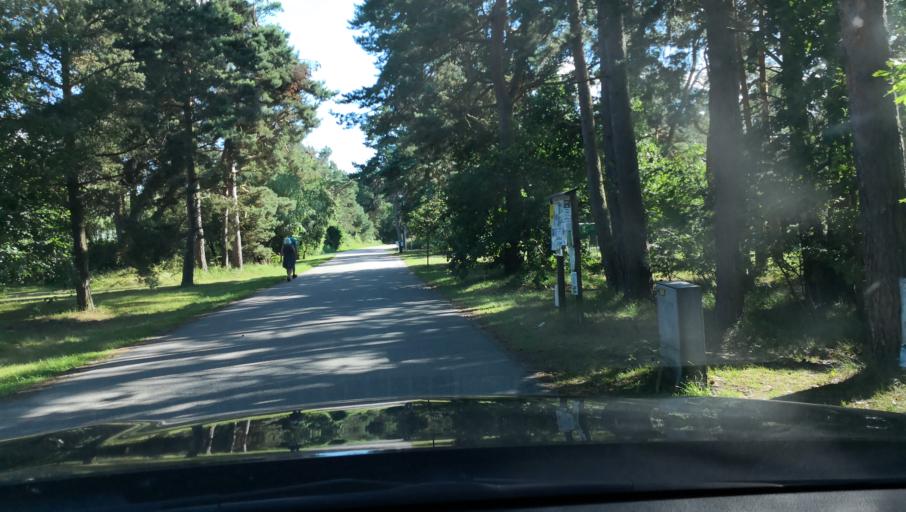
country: SE
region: Skane
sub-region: Simrishamns Kommun
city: Kivik
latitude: 55.7835
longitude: 14.1949
